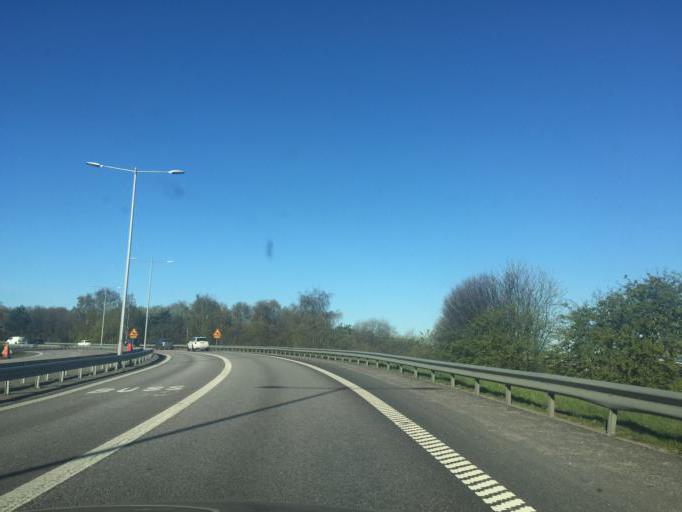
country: SE
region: Vaestra Goetaland
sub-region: Goteborg
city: Majorna
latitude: 57.6872
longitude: 11.9022
